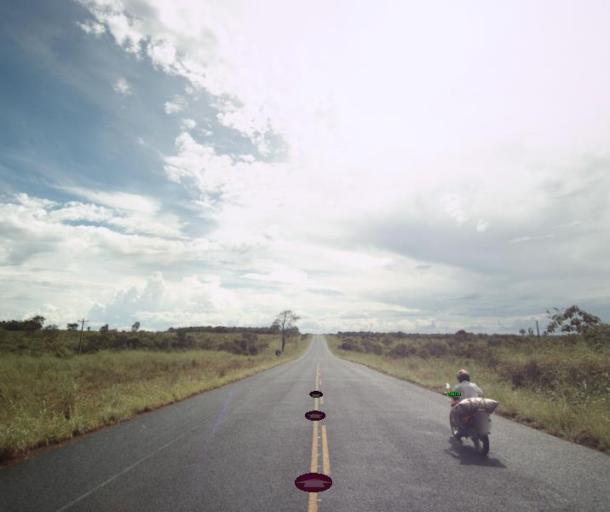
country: BR
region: Goias
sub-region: Sao Miguel Do Araguaia
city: Sao Miguel do Araguaia
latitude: -13.2977
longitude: -50.3349
